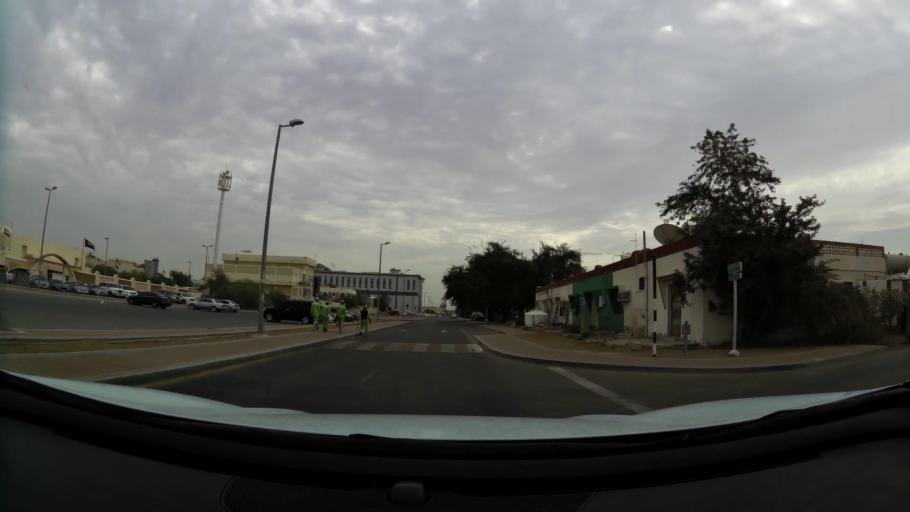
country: AE
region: Abu Dhabi
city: Al Ain
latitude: 24.2281
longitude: 55.7406
